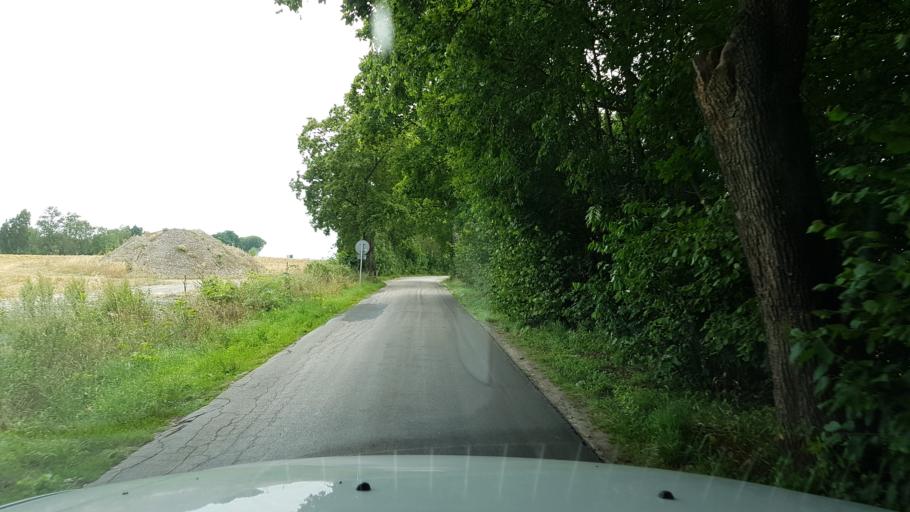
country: PL
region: West Pomeranian Voivodeship
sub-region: Koszalin
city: Koszalin
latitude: 54.1574
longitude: 16.0760
